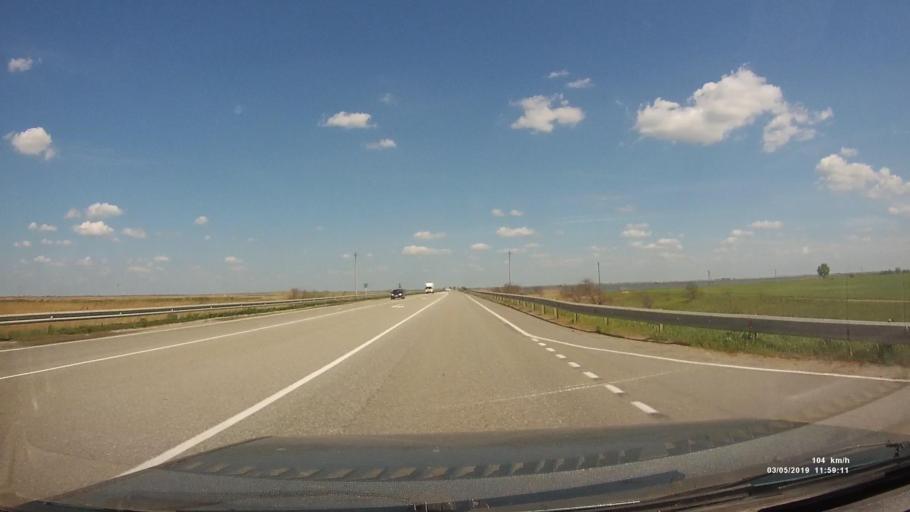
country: RU
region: Rostov
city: Bagayevskaya
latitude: 47.2313
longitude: 40.3278
